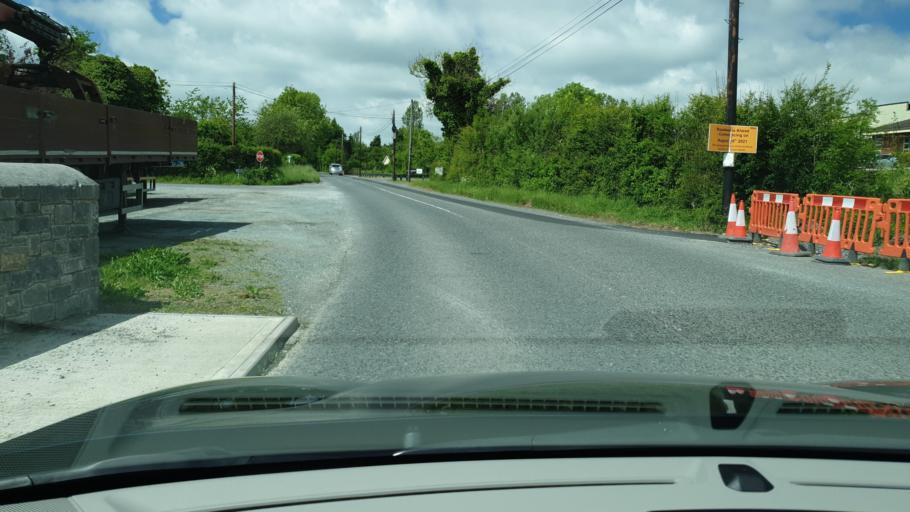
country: IE
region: Ulster
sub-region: An Cabhan
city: Kingscourt
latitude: 53.8982
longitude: -6.7688
